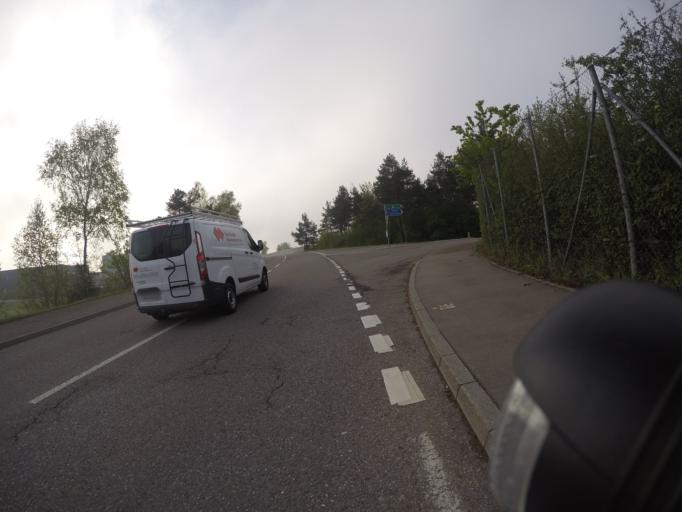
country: CH
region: Zurich
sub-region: Bezirk Pfaeffikon
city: Tagelswangen
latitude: 47.4386
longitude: 8.6821
